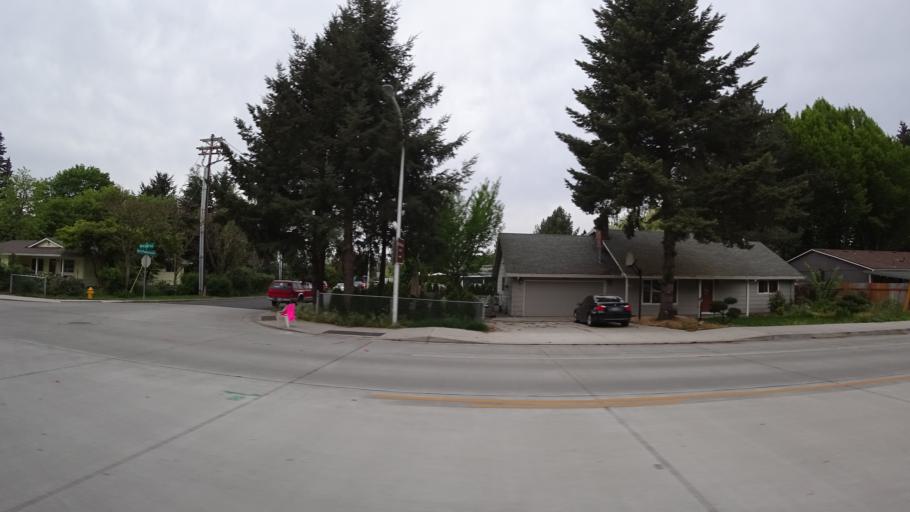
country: US
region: Oregon
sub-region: Washington County
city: Hillsboro
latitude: 45.5239
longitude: -122.9543
